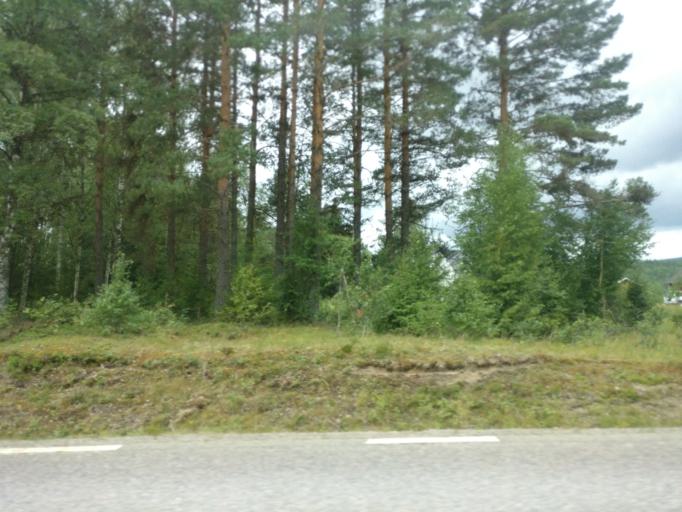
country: SE
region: Vaermland
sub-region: Torsby Kommun
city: Torsby
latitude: 60.7629
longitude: 12.7622
